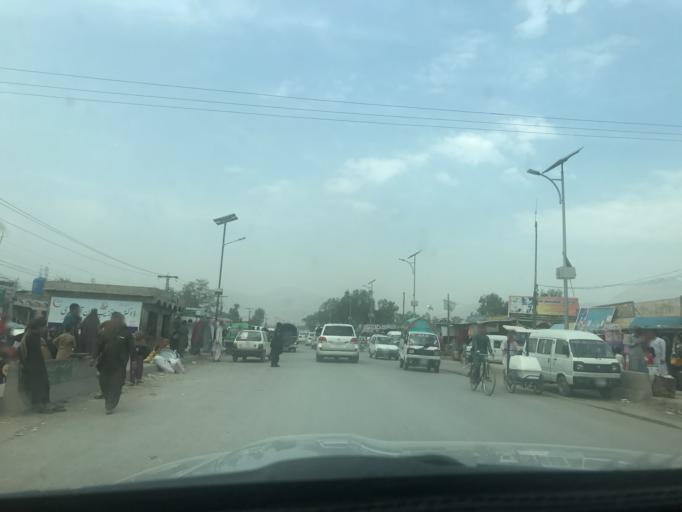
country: PK
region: Khyber Pakhtunkhwa
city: Peshawar
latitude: 34.0023
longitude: 71.3791
